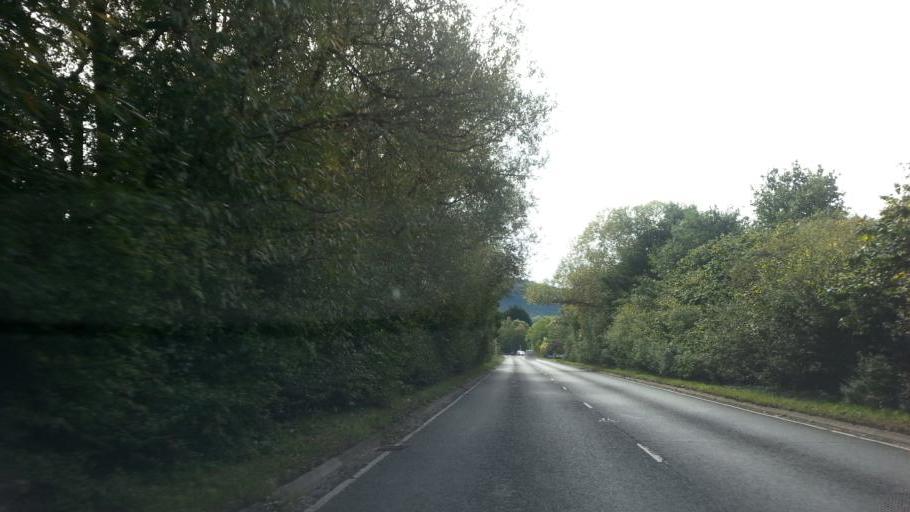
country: GB
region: England
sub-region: Herefordshire
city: Ross on Wye
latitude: 51.9170
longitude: -2.5703
